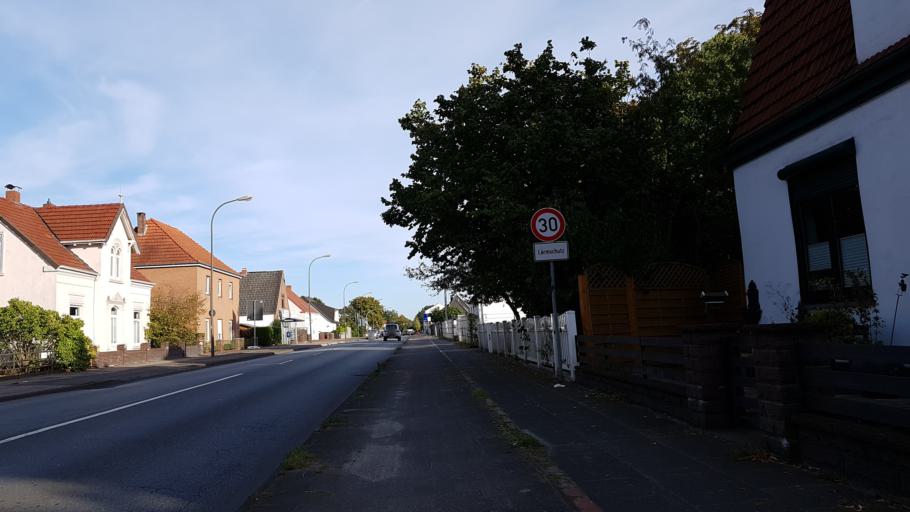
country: DE
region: Lower Saxony
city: Oyten
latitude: 53.0339
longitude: 8.9545
